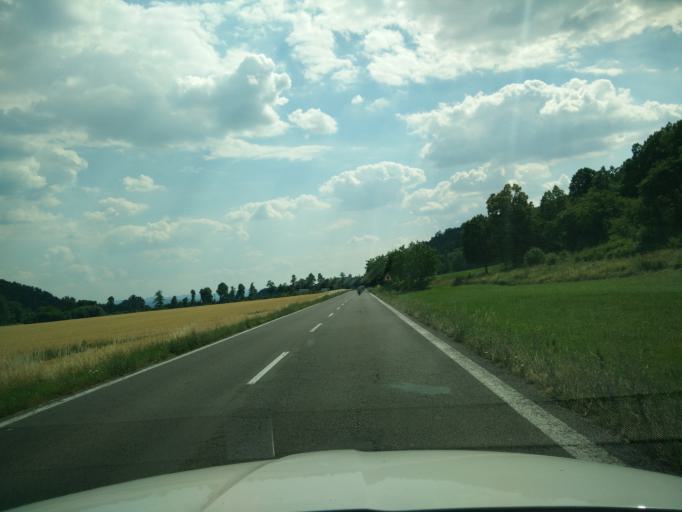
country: SK
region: Nitriansky
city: Partizanske
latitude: 48.6985
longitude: 18.3874
